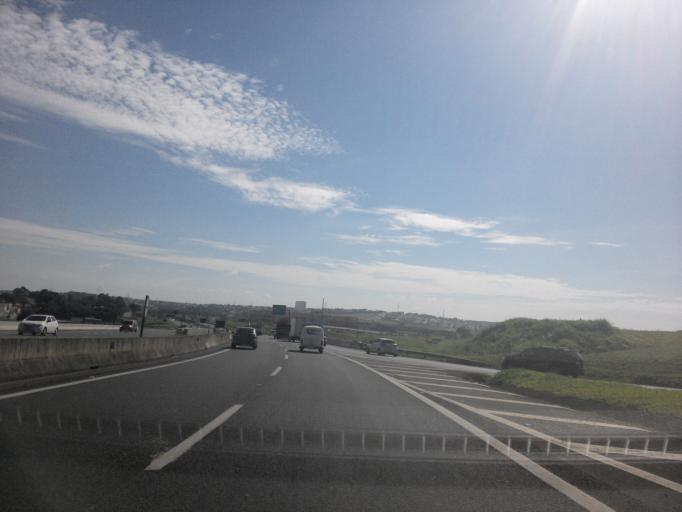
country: BR
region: Sao Paulo
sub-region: Campinas
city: Campinas
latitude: -22.8452
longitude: -47.0391
